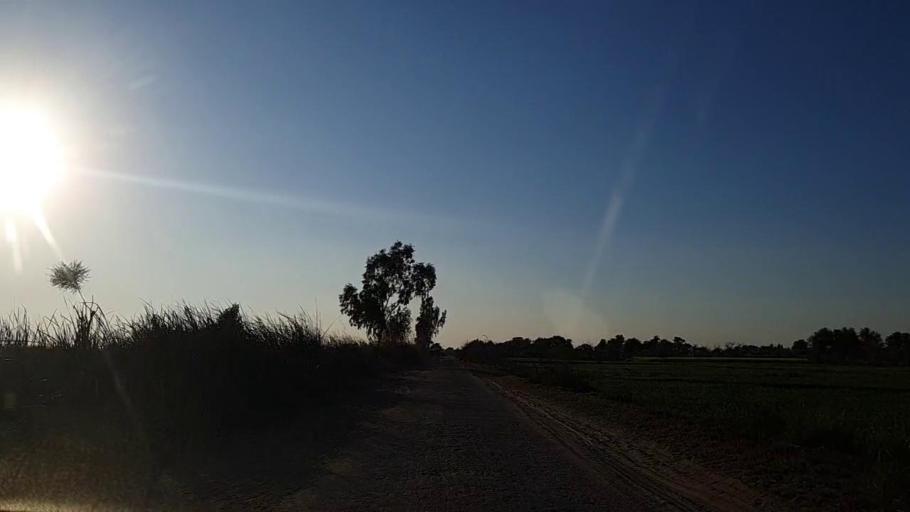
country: PK
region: Sindh
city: Khadro
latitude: 26.2790
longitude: 68.8429
